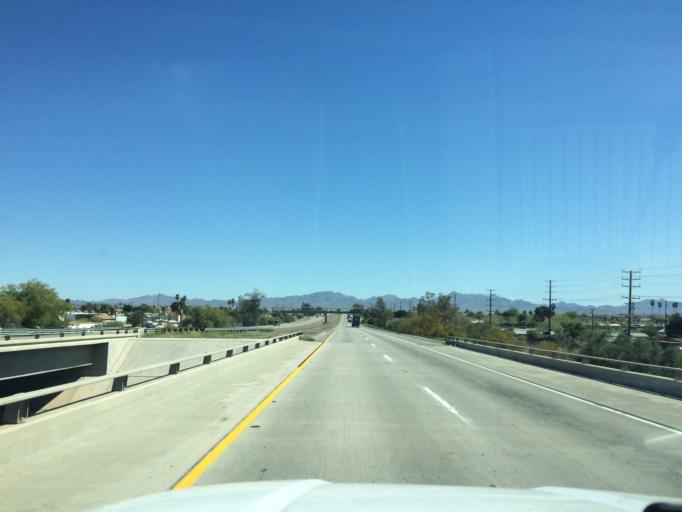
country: US
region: California
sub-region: Riverside County
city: Blythe
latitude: 33.6070
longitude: -114.5972
